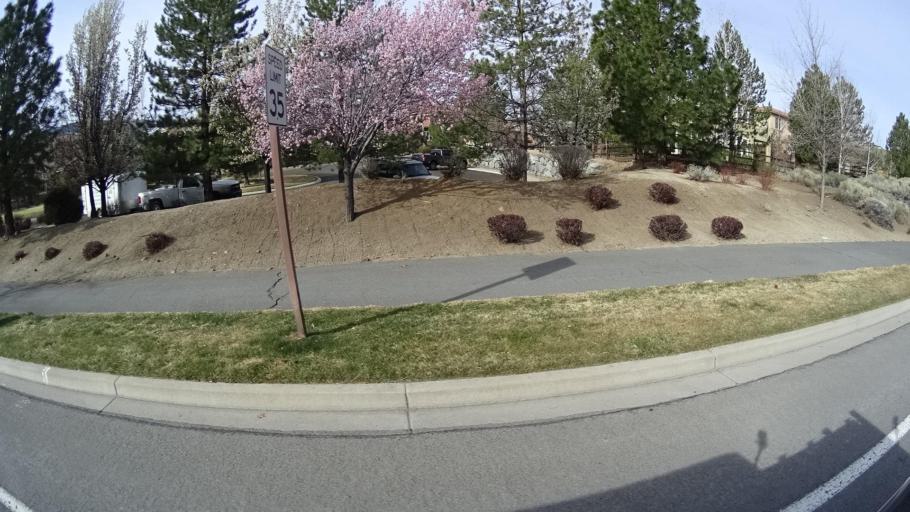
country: US
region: Nevada
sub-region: Washoe County
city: Mogul
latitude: 39.5360
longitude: -119.9242
